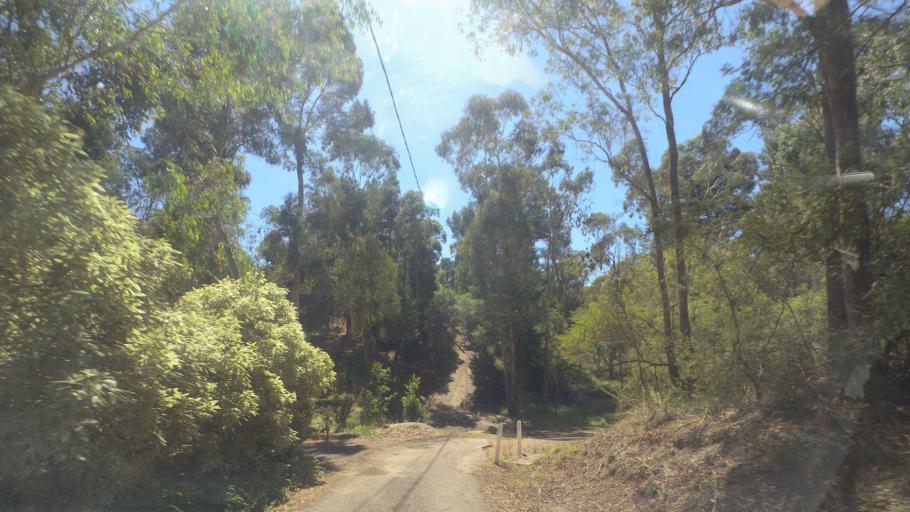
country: AU
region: Victoria
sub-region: Manningham
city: Donvale
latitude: -37.7861
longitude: 145.1913
